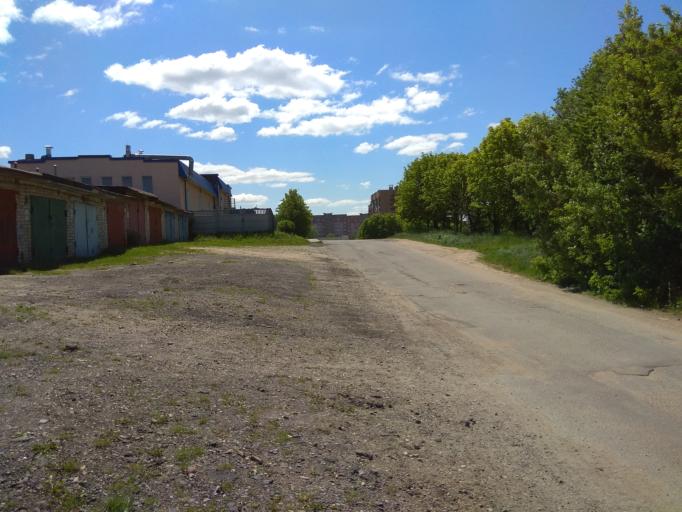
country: BY
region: Grodnenskaya
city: Hrodna
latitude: 53.7121
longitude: 23.8019
